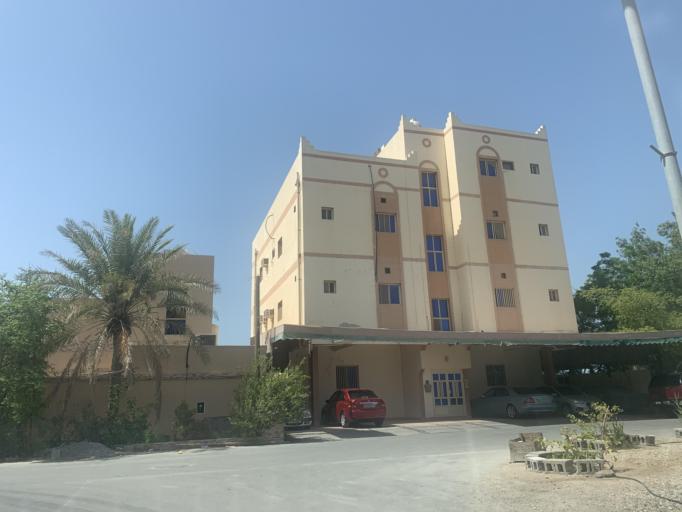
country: BH
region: Manama
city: Jidd Hafs
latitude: 26.2350
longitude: 50.5106
